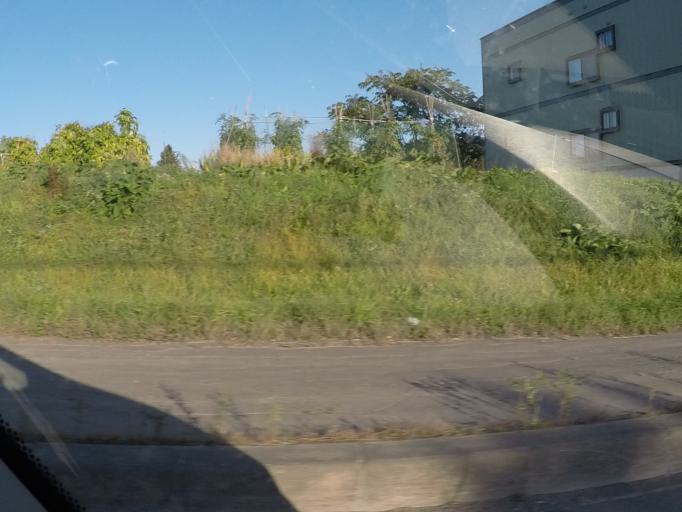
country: JP
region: Hokkaido
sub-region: Asahikawa-shi
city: Asahikawa
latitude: 43.6020
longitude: 142.4764
